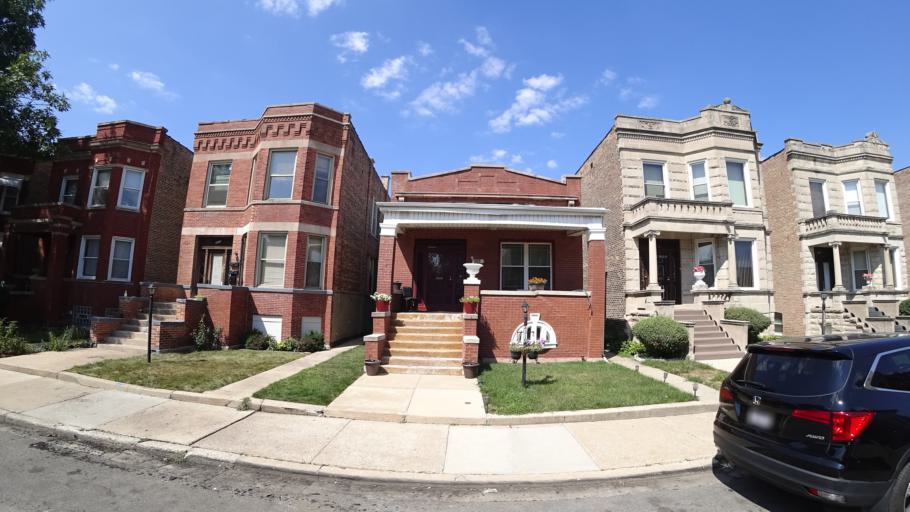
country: US
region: Illinois
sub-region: Cook County
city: Cicero
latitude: 41.8525
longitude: -87.7326
